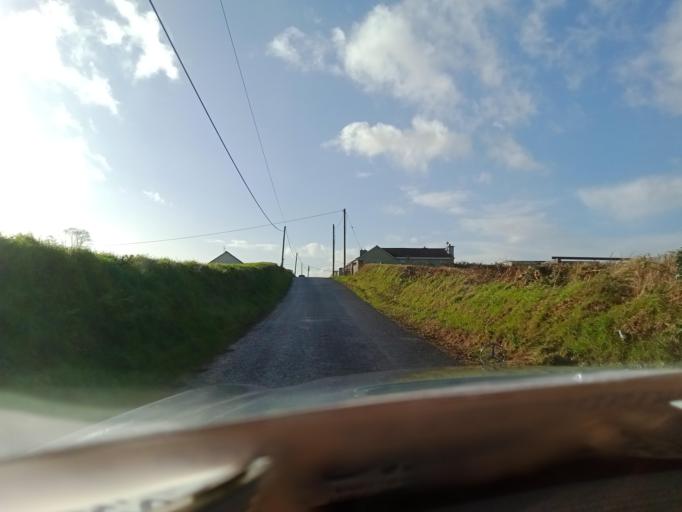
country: IE
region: Munster
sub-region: Waterford
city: Portlaw
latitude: 52.3267
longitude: -7.2864
